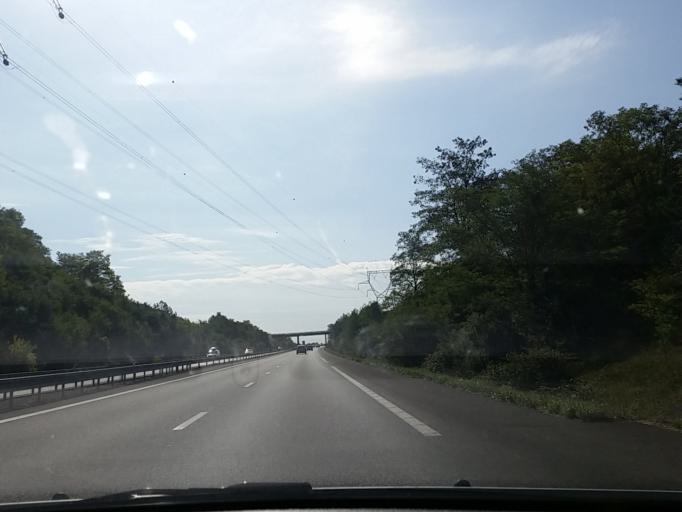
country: FR
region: Centre
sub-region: Departement du Cher
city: La Chapelle-Saint-Ursin
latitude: 47.0583
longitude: 2.3071
